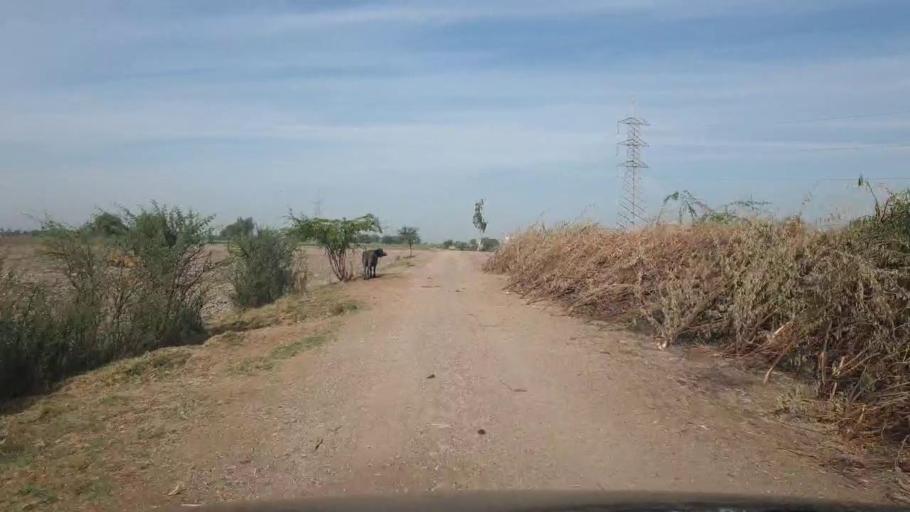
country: PK
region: Sindh
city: Umarkot
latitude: 25.3675
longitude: 69.6483
